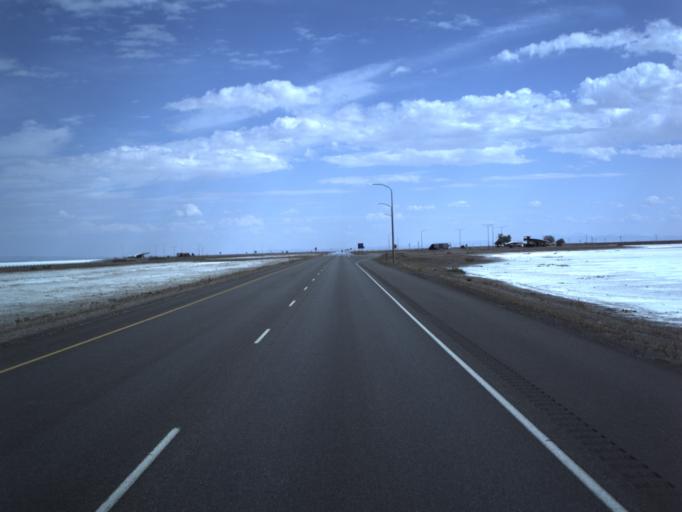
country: US
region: Utah
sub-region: Tooele County
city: Wendover
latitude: 40.7387
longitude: -113.8639
